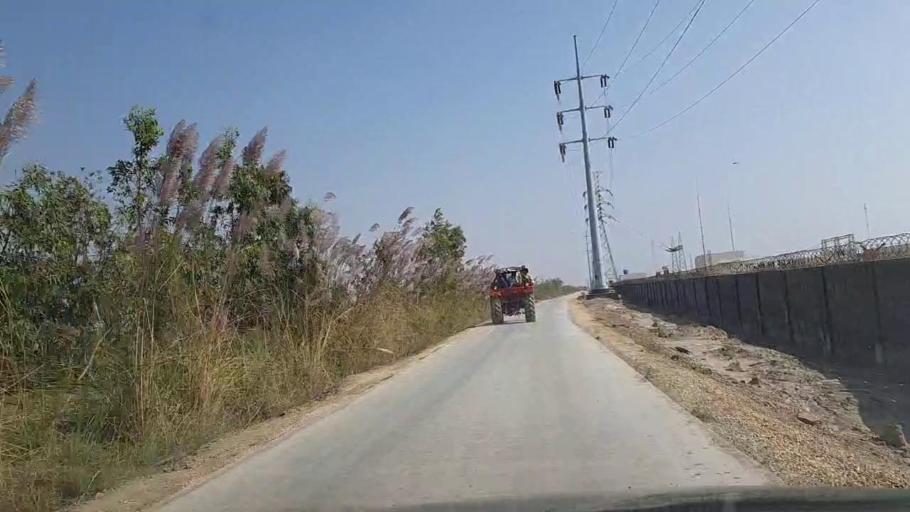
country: PK
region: Sindh
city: Gharo
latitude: 24.7217
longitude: 67.5342
